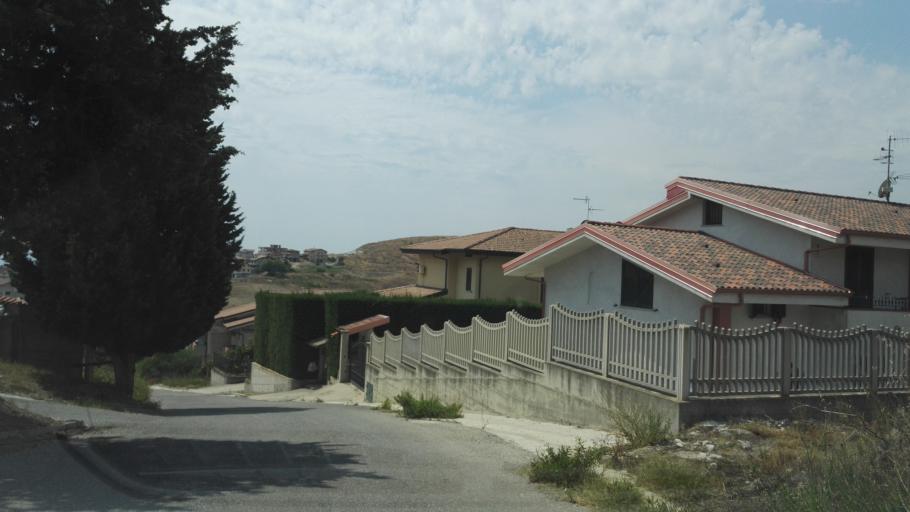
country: IT
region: Calabria
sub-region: Provincia di Reggio Calabria
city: Riace Marina
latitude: 38.3915
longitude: 16.5241
